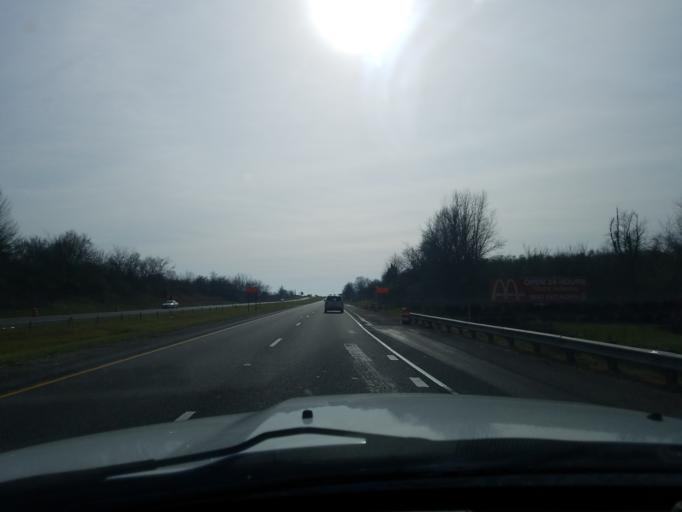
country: US
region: Indiana
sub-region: Delaware County
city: Yorktown
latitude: 40.2136
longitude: -85.5611
